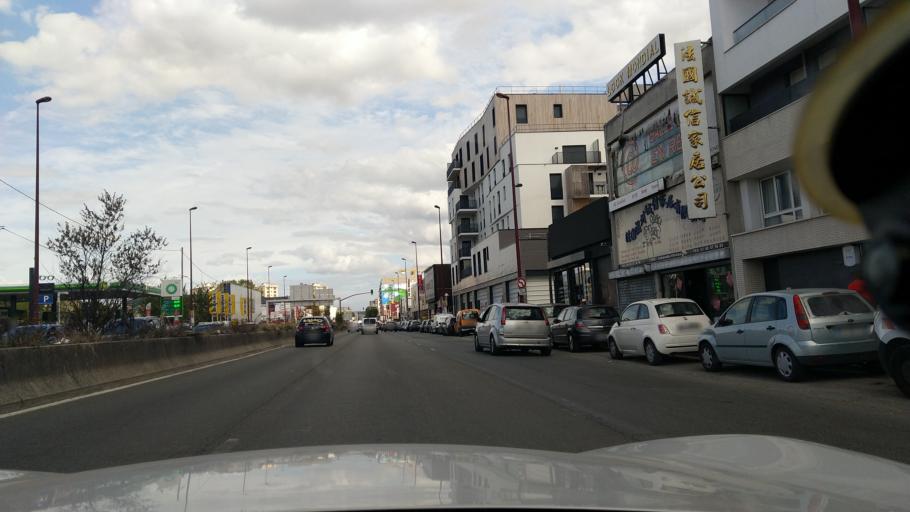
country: FR
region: Ile-de-France
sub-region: Departement de Seine-Saint-Denis
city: Bondy
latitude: 48.9064
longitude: 2.4842
